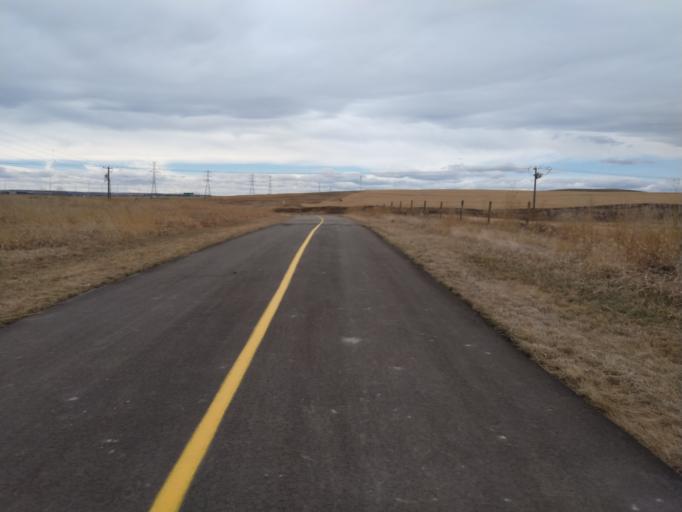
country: CA
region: Alberta
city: Airdrie
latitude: 51.1774
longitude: -114.0467
